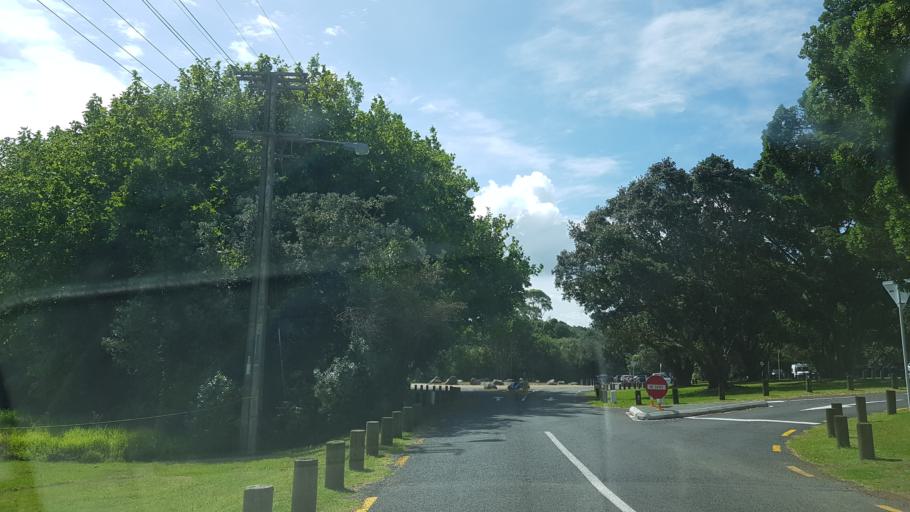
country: NZ
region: Auckland
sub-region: Auckland
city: Rothesay Bay
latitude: -36.6840
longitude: 174.7482
